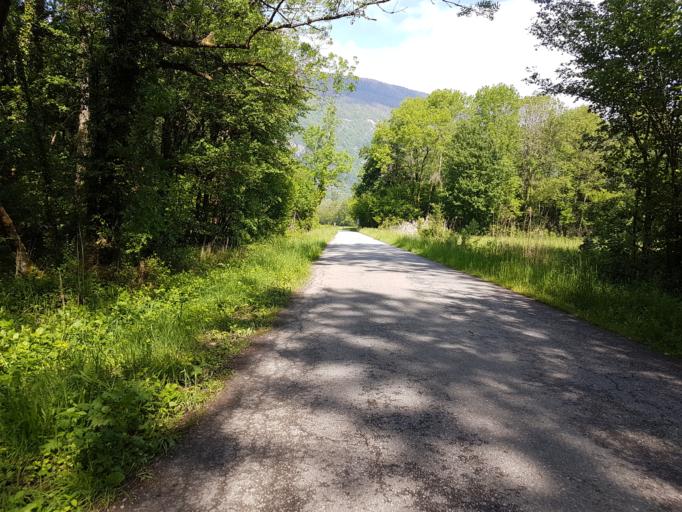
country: FR
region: Rhone-Alpes
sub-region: Departement de l'Ain
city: Culoz
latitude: 45.8527
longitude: 5.8152
